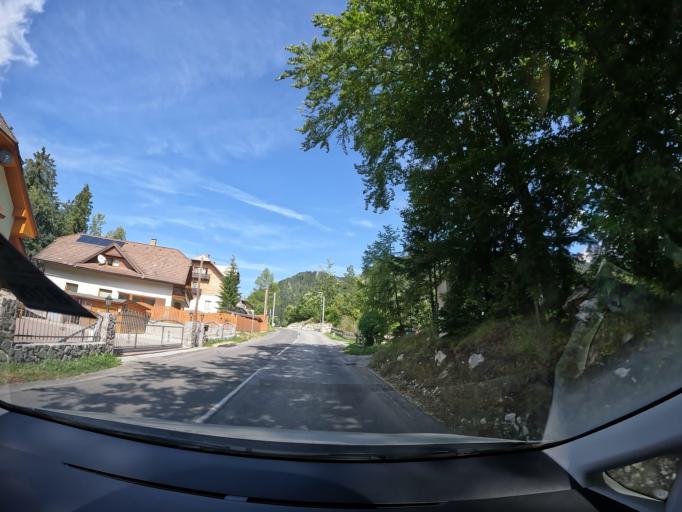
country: AT
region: Carinthia
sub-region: Politischer Bezirk Klagenfurt Land
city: Moosburg
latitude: 46.6674
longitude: 14.1274
